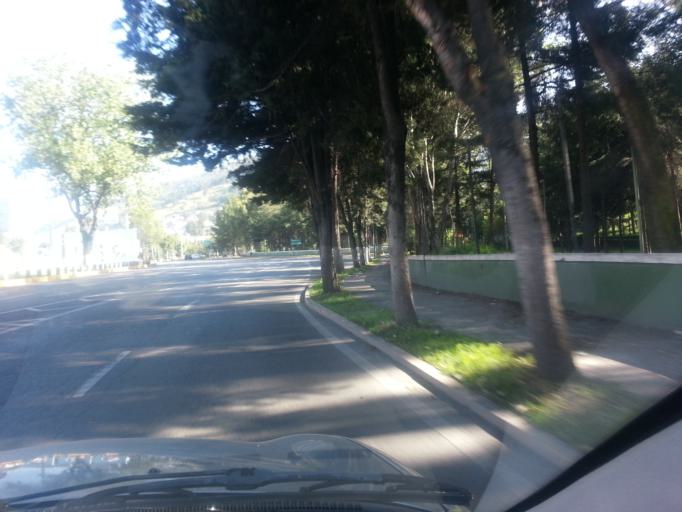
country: MX
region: Mexico
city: San Buenaventura
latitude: 19.2840
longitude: -99.6804
